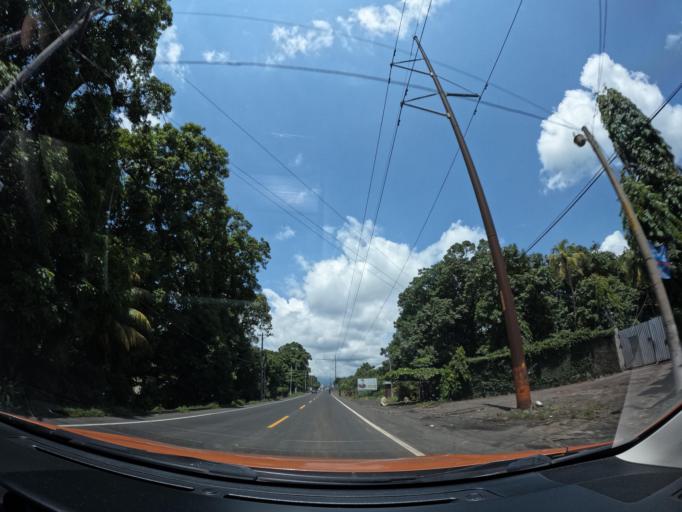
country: GT
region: Escuintla
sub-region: Municipio de Escuintla
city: Escuintla
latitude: 14.2707
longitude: -90.7923
